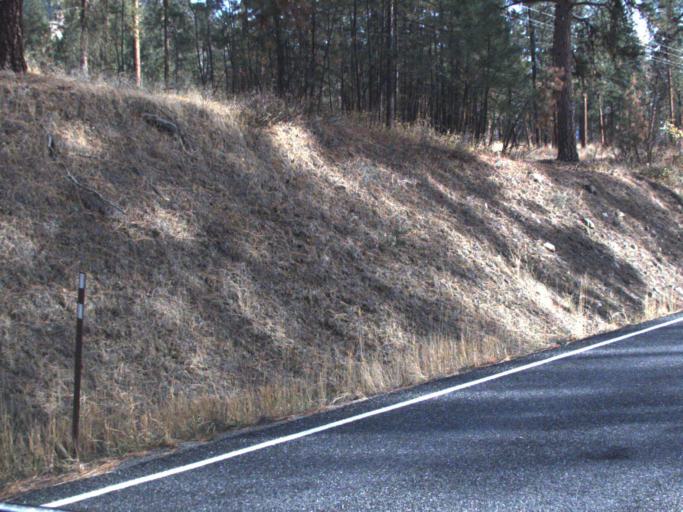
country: US
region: Washington
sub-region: Stevens County
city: Kettle Falls
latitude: 48.2921
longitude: -118.1424
